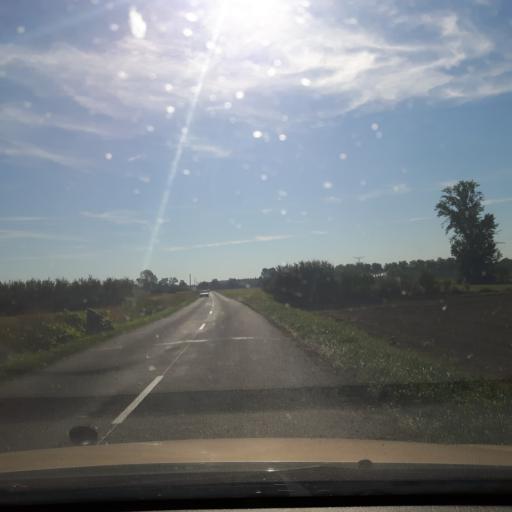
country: FR
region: Midi-Pyrenees
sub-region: Departement de la Haute-Garonne
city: Villeneuve-les-Bouloc
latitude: 43.7591
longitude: 1.4279
